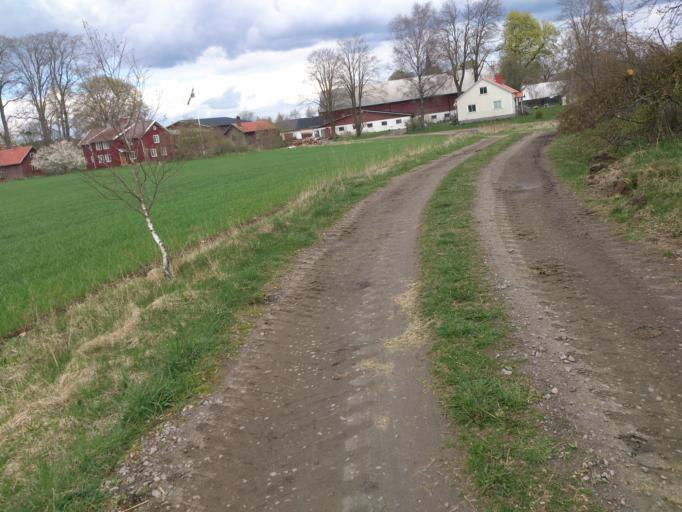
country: SE
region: Vaestra Goetaland
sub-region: Ulricehamns Kommun
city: Ulricehamn
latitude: 57.9550
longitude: 13.5175
